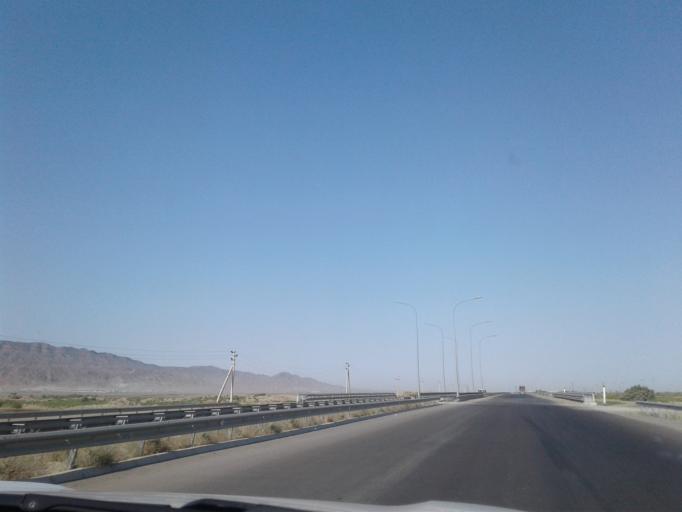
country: TM
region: Balkan
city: Gazanjyk
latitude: 39.2499
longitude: 55.6153
